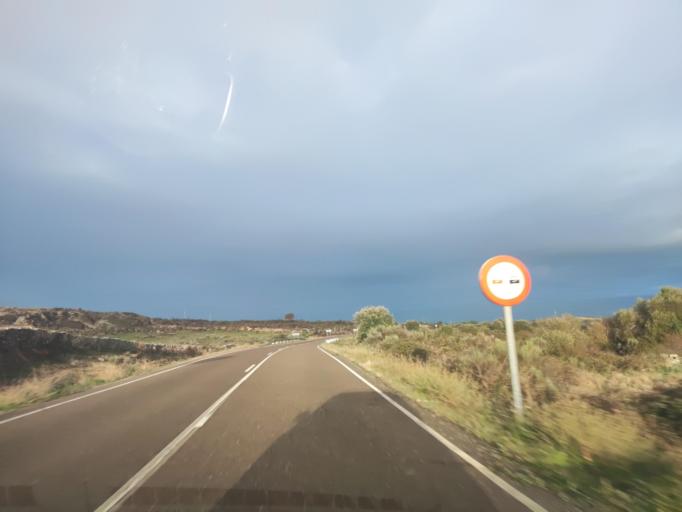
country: ES
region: Castille and Leon
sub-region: Provincia de Salamanca
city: San Felices de los Gallegos
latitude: 40.8262
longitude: -6.6822
